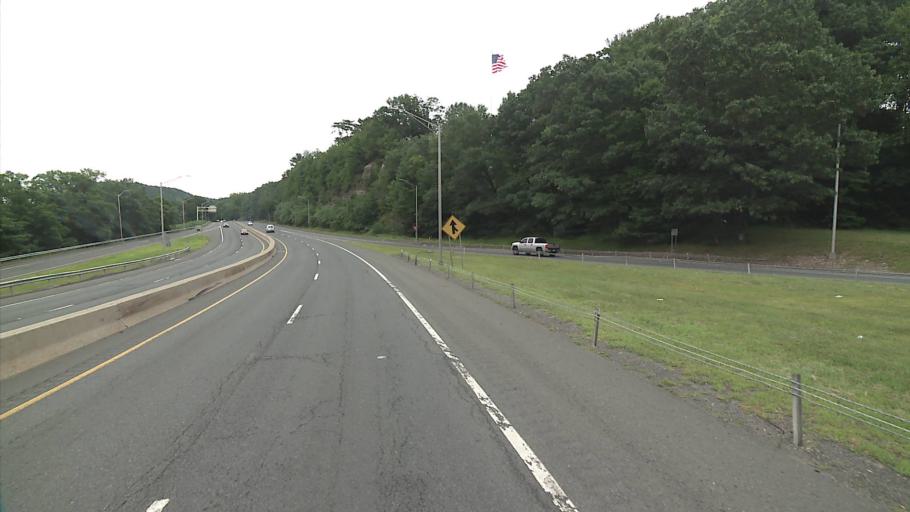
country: US
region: Connecticut
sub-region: New Haven County
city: Seymour
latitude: 41.3989
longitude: -73.0690
